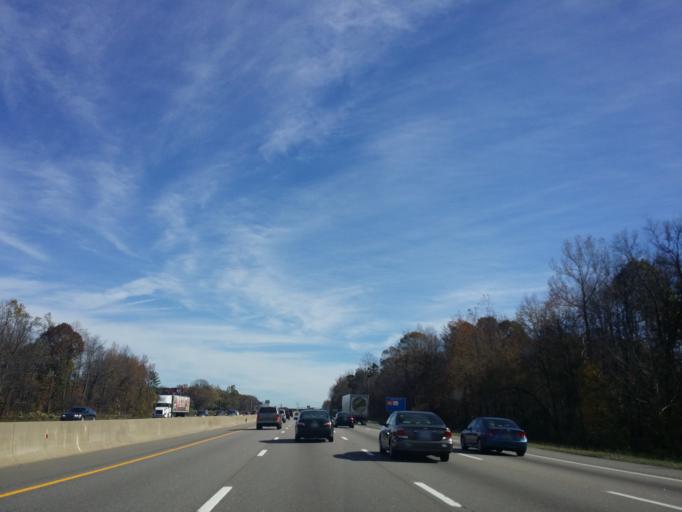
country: US
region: North Carolina
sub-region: Alamance County
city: Mebane
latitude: 36.0781
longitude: -79.2393
